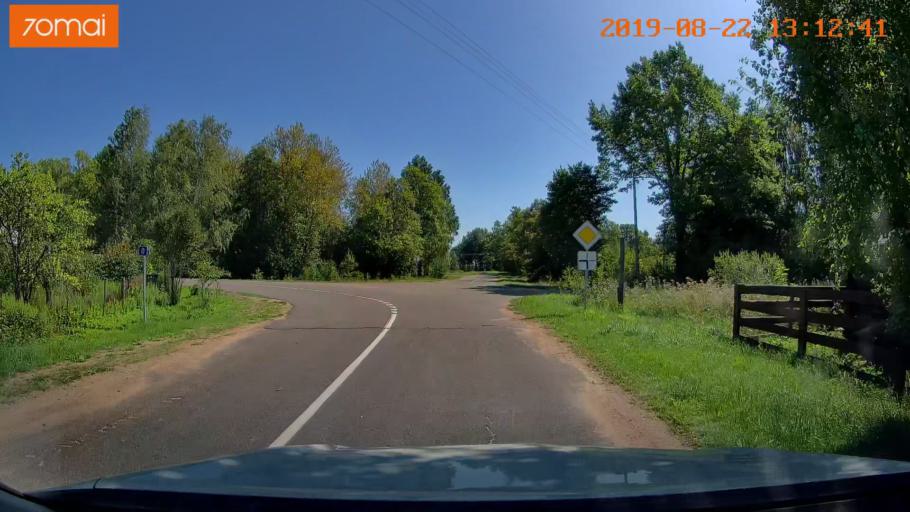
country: BY
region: Minsk
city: Prawdzinski
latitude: 53.2677
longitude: 27.8668
